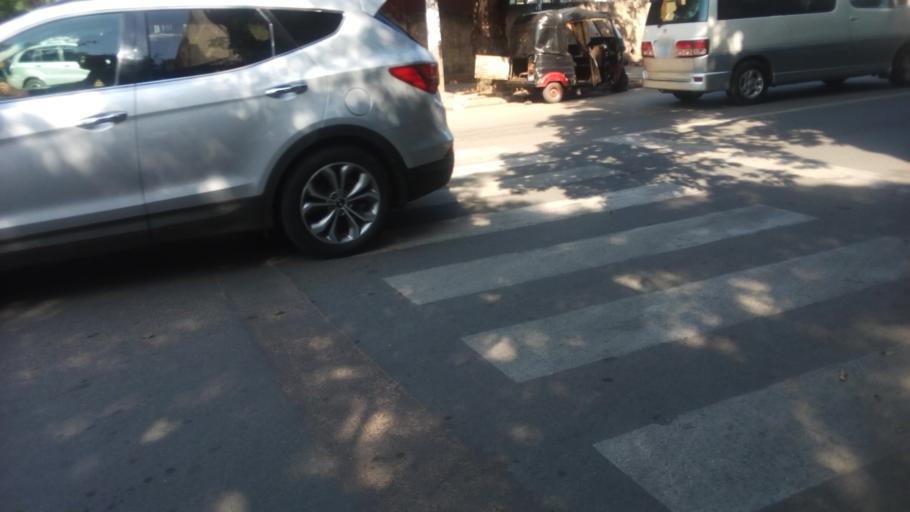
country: MZ
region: Maputo City
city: Maputo
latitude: -25.9602
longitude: 32.5751
